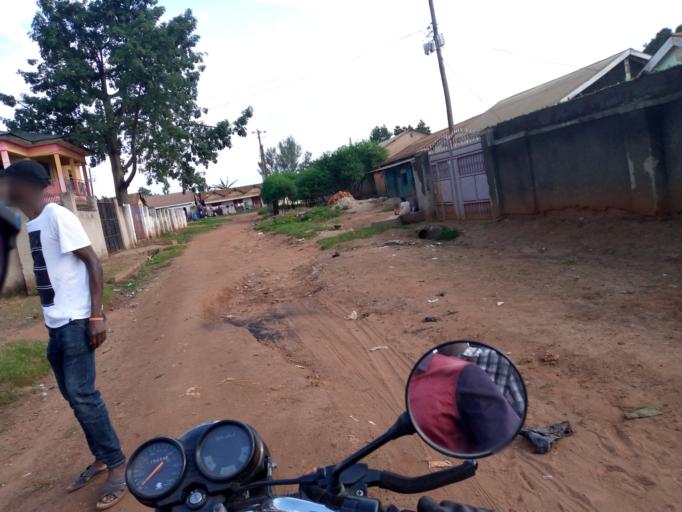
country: UG
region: Eastern Region
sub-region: Mbale District
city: Mbale
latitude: 1.0700
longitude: 34.1623
